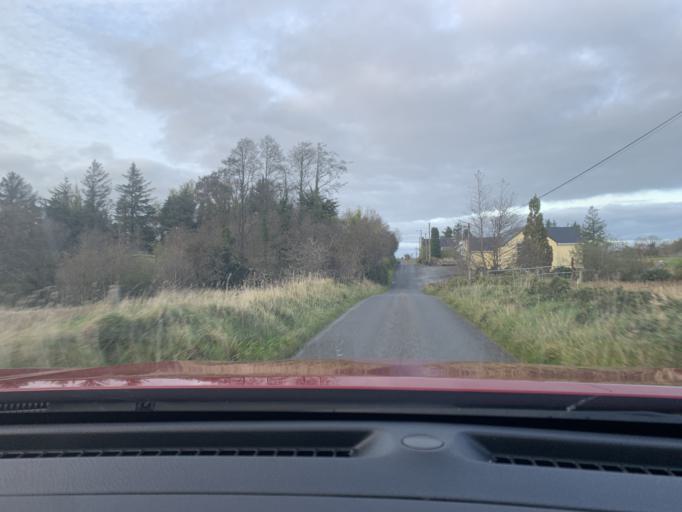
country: IE
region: Connaught
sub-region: Roscommon
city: Ballaghaderreen
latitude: 53.9743
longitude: -8.6216
